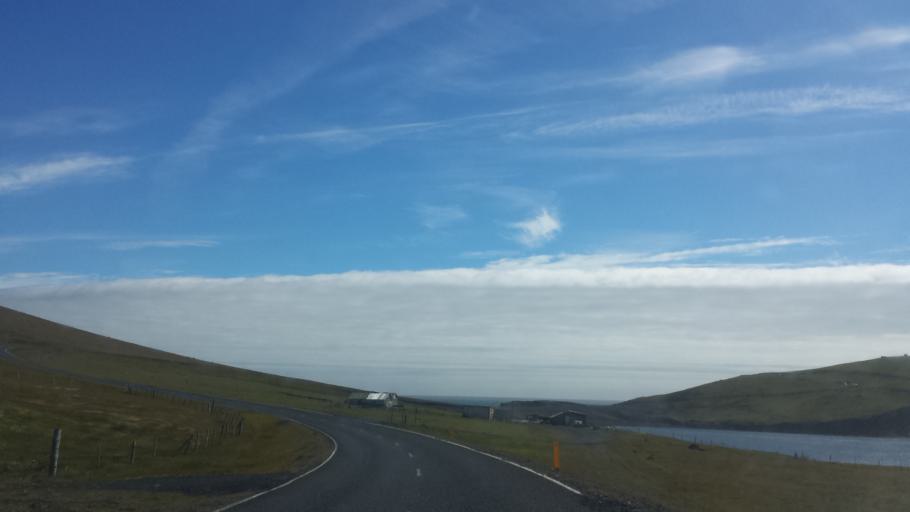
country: IS
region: South
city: Vestmannaeyjar
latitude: 63.4145
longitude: -20.2857
